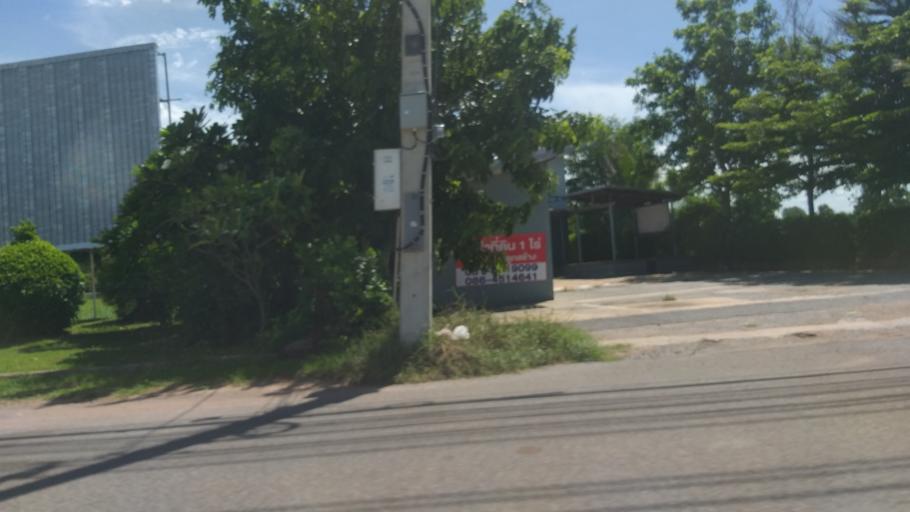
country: TH
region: Khon Kaen
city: Ban Fang
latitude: 16.4585
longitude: 102.6313
